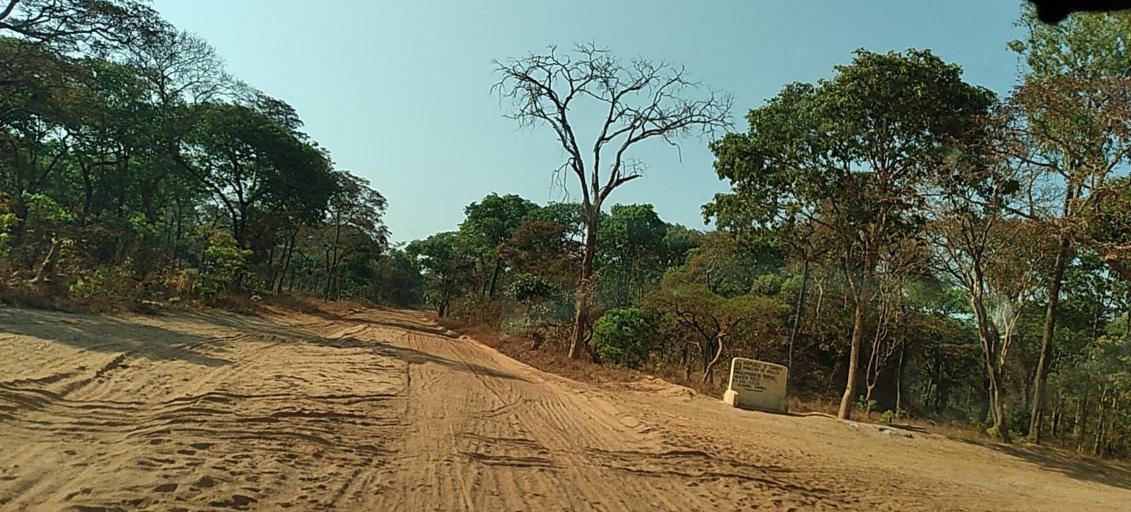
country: ZM
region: North-Western
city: Kasempa
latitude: -13.6839
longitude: 26.0262
